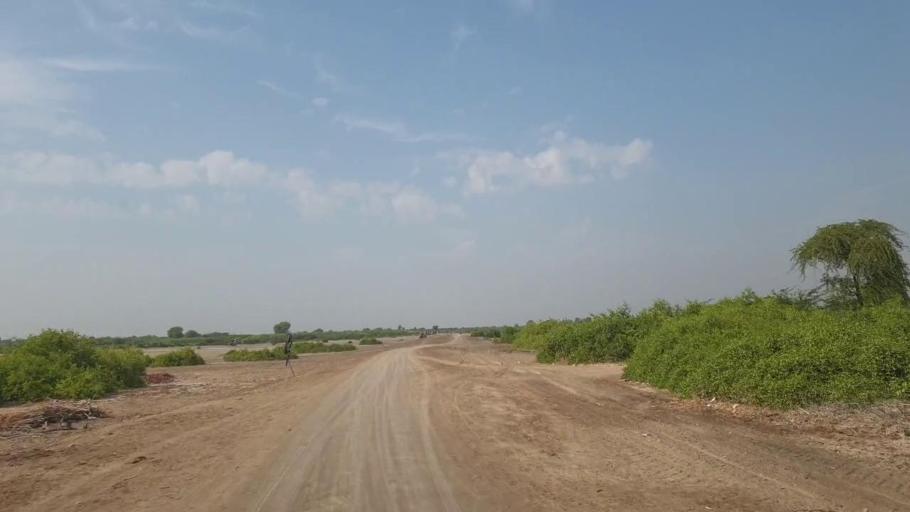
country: PK
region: Sindh
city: Digri
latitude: 25.0307
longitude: 69.0709
